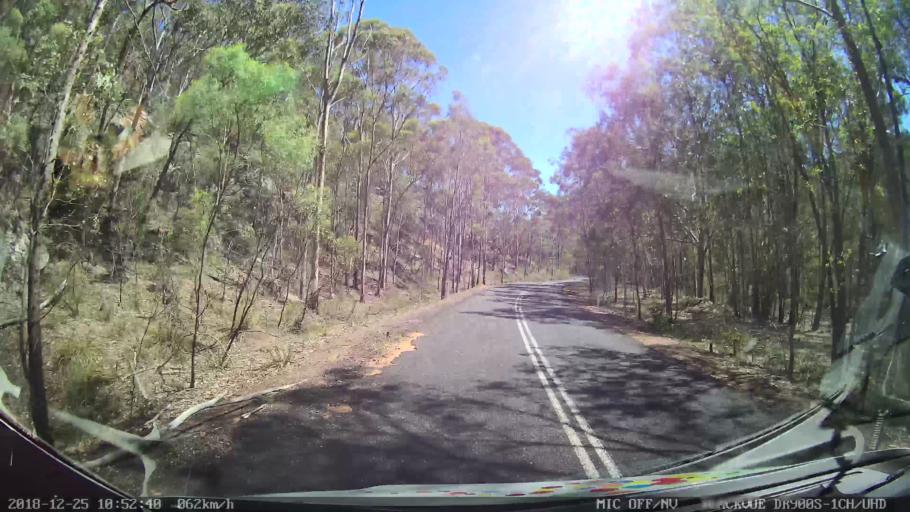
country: AU
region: New South Wales
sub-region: Upper Hunter Shire
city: Merriwa
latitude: -32.4266
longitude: 150.2734
